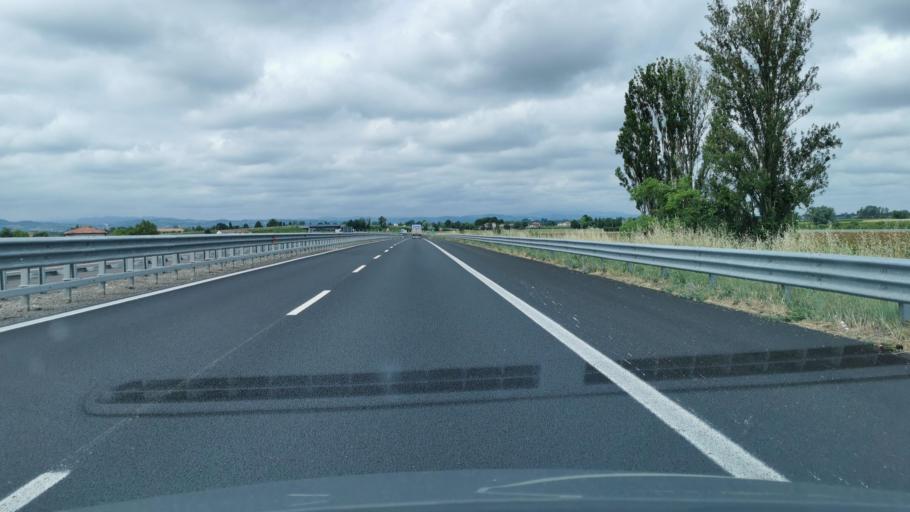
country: IT
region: Emilia-Romagna
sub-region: Provincia di Ravenna
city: Solarolo
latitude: 44.3685
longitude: 11.8391
